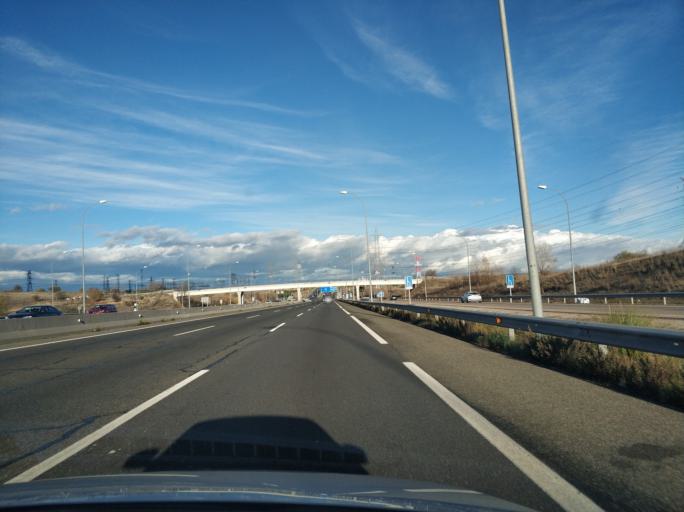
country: ES
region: Madrid
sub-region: Provincia de Madrid
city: San Sebastian de los Reyes
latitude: 40.5558
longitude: -3.6040
